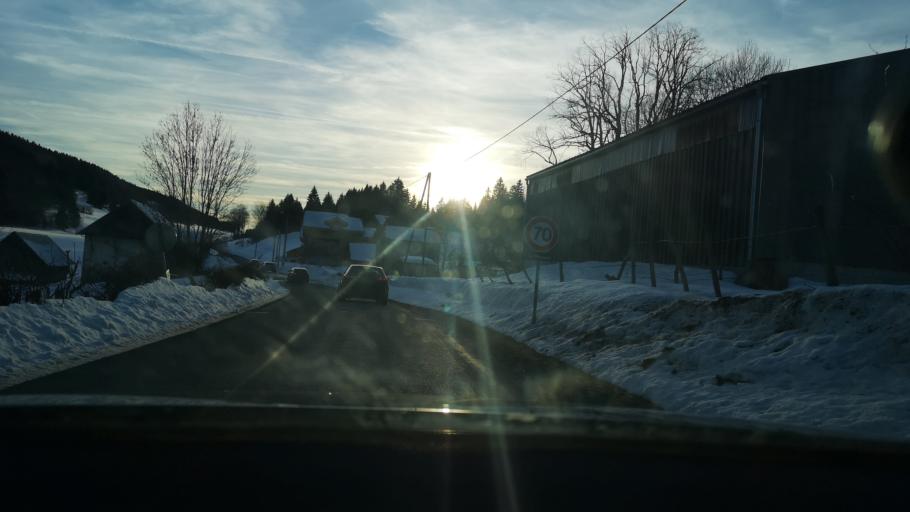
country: FR
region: Franche-Comte
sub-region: Departement du Doubs
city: Gilley
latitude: 46.9875
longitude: 6.5100
